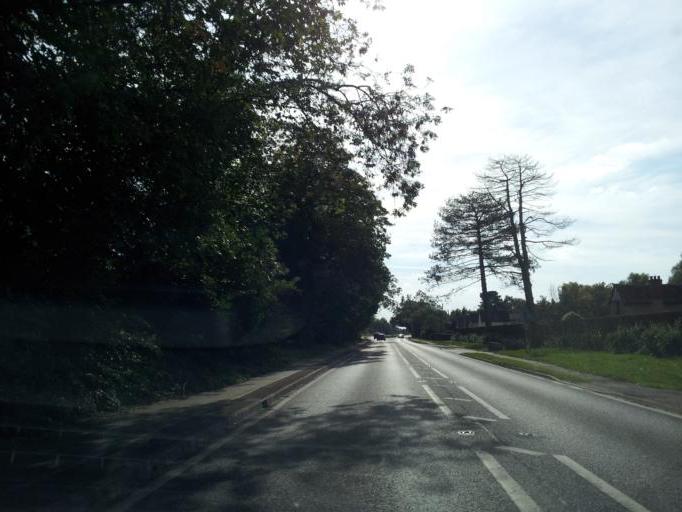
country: GB
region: England
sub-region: Cambridgeshire
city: Waterbeach
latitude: 52.2669
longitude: 0.1802
